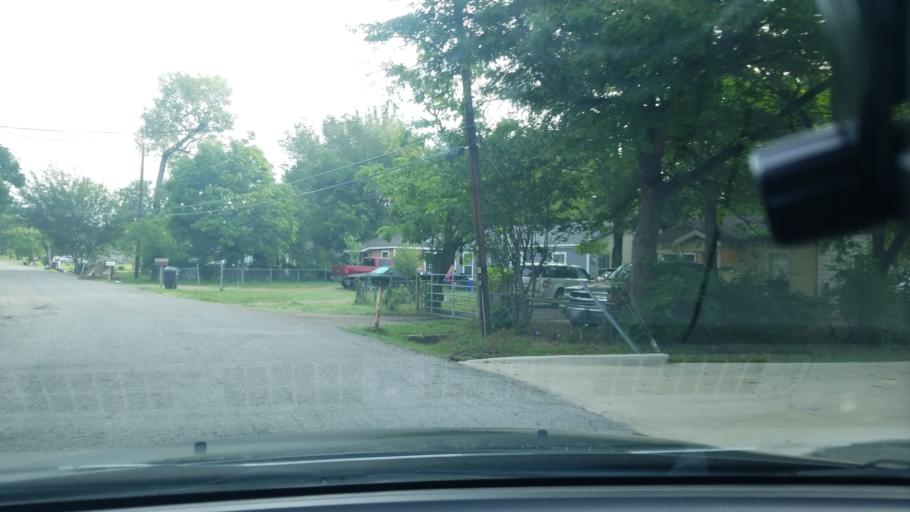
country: US
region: Texas
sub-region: Dallas County
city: Balch Springs
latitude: 32.7592
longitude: -96.6409
